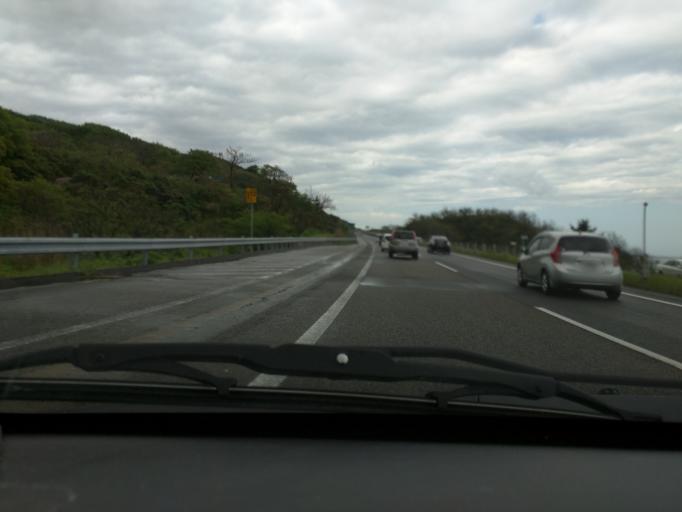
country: JP
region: Niigata
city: Kashiwazaki
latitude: 37.3115
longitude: 138.4274
